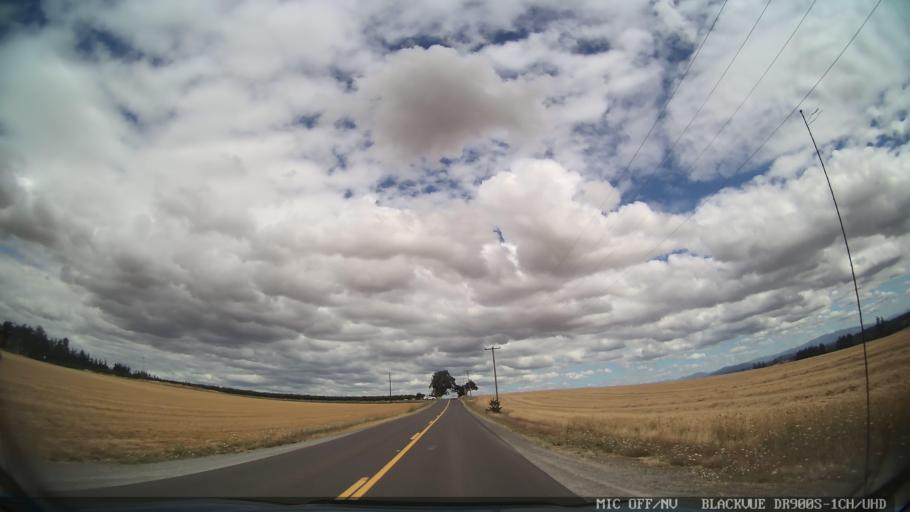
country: US
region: Oregon
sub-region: Marion County
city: Aumsville
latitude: 44.8654
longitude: -122.8408
